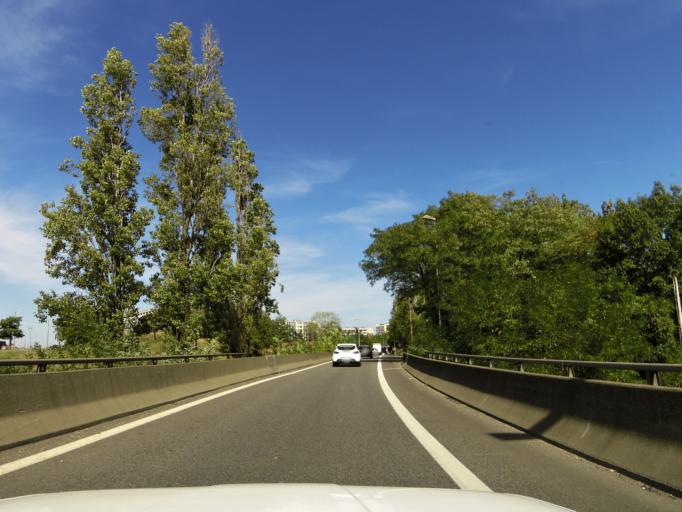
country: FR
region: Rhone-Alpes
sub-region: Departement du Rhone
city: Bron
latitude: 45.7271
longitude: 4.8972
